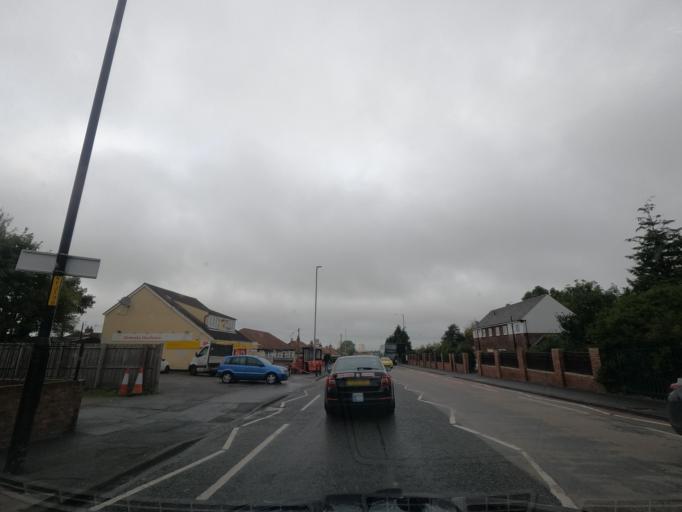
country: GB
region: England
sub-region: Middlesbrough
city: Nunthorpe
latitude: 54.5506
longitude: -1.1803
